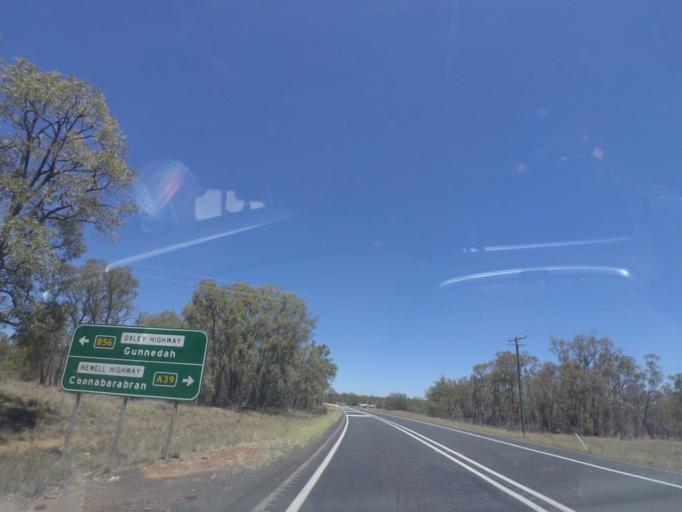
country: AU
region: New South Wales
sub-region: Warrumbungle Shire
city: Coonabarabran
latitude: -31.2426
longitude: 149.3131
